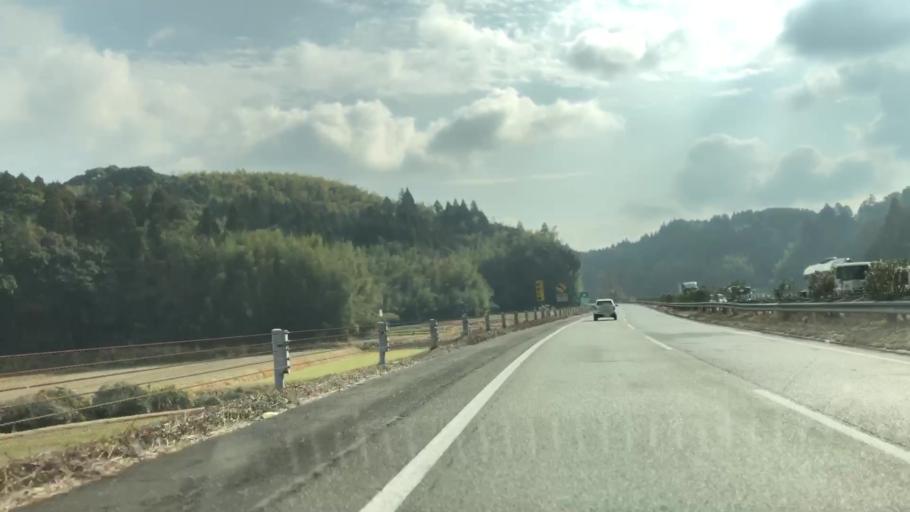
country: JP
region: Kumamoto
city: Yamaga
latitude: 33.0270
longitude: 130.5769
